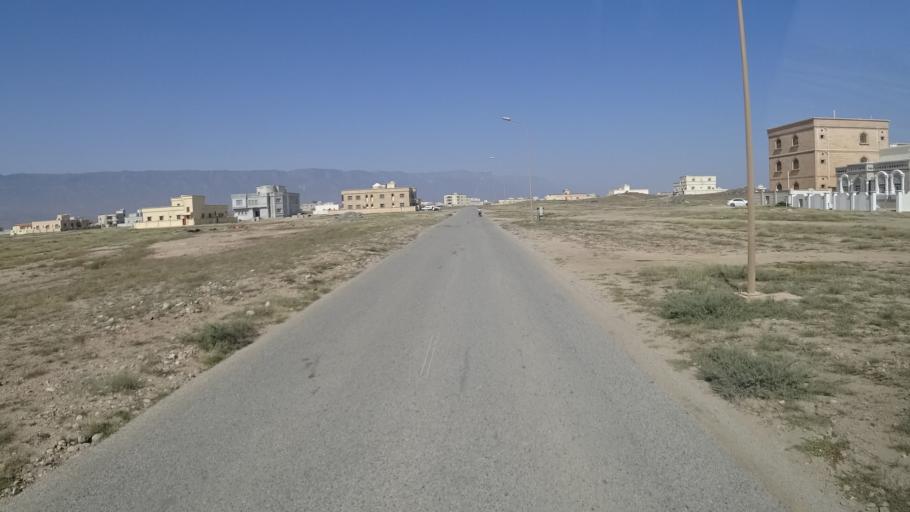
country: OM
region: Zufar
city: Salalah
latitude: 16.9902
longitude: 54.7168
